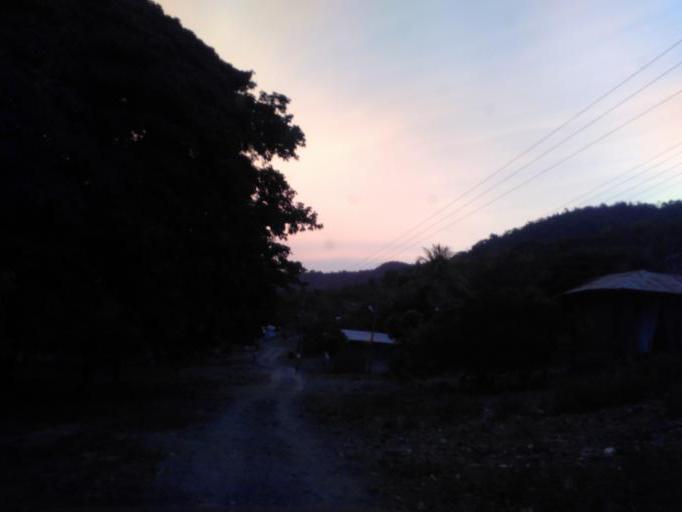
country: GH
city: Bekwai
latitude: 6.5069
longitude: -1.4454
